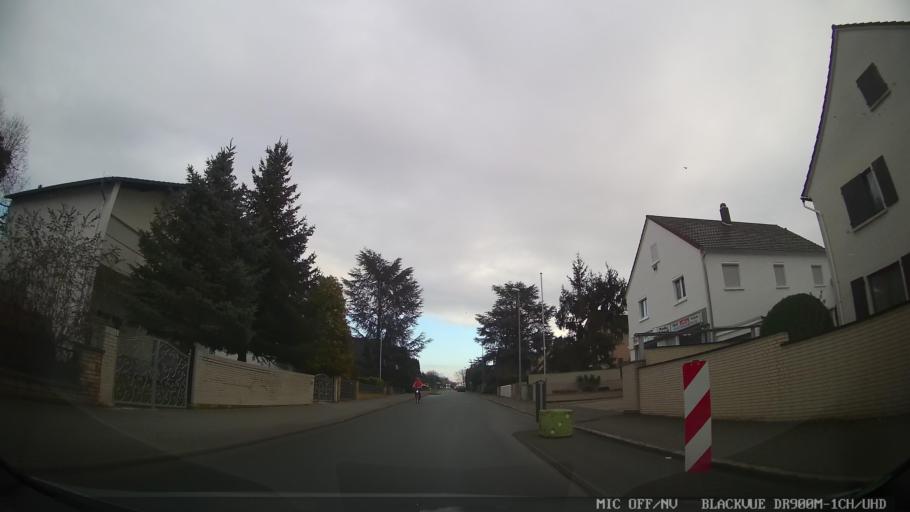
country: DE
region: Rheinland-Pfalz
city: Kongernheim
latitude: 49.8445
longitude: 8.2493
